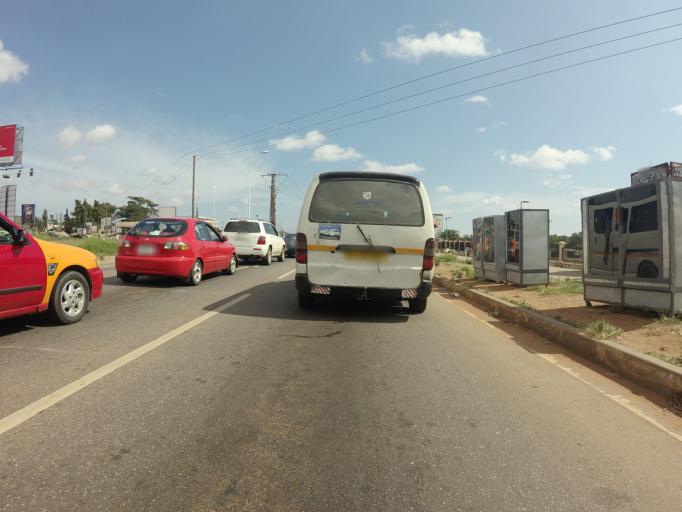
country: GH
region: Greater Accra
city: Medina Estates
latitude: 5.7093
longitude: -0.1715
